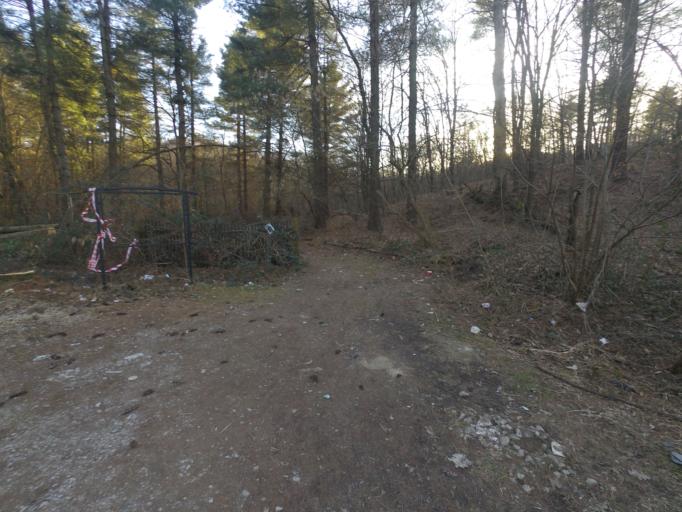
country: HR
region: Karlovacka
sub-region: Grad Karlovac
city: Karlovac
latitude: 45.4779
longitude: 15.5336
